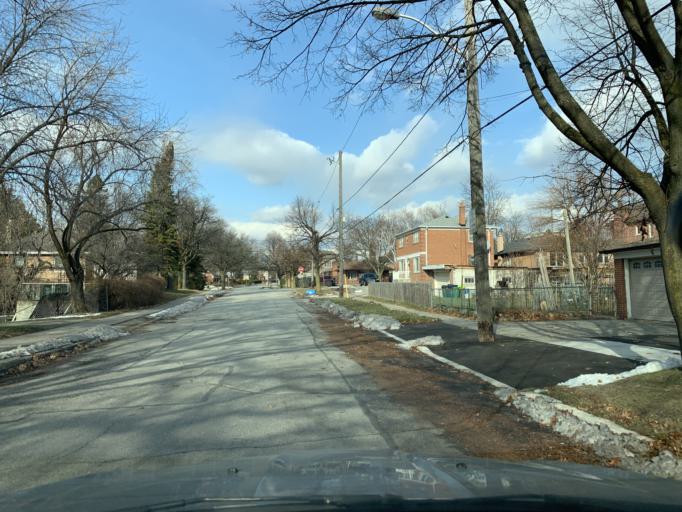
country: CA
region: Ontario
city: Toronto
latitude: 43.7004
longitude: -79.4806
